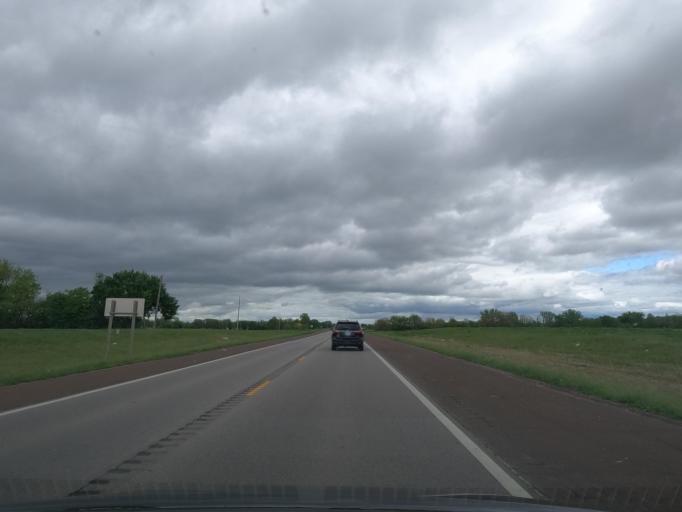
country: US
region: Kansas
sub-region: Crawford County
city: Pittsburg
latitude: 37.3382
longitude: -94.6274
